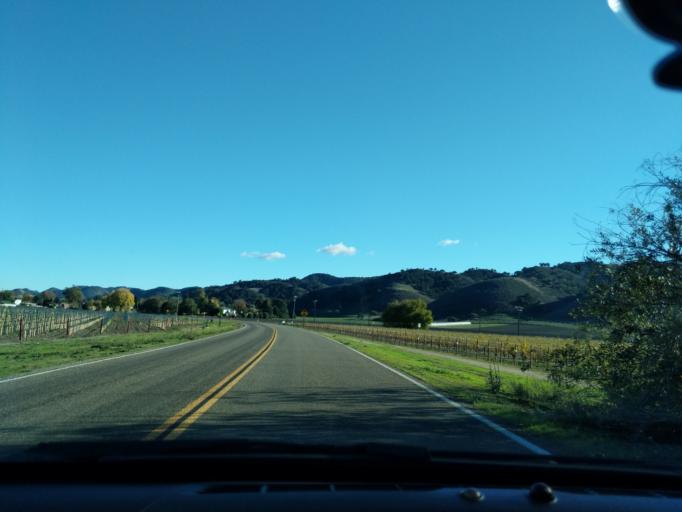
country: US
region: California
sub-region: Santa Barbara County
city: Los Alamos
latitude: 34.7471
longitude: -120.2891
